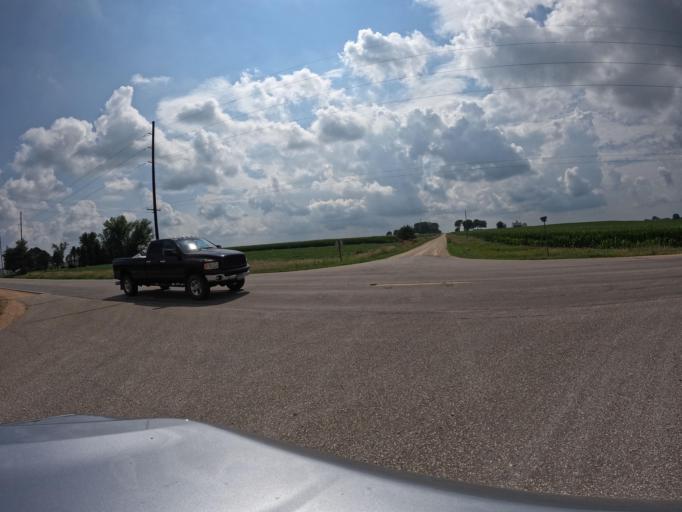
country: US
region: Iowa
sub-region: Clinton County
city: Camanche
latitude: 41.7720
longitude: -90.3548
